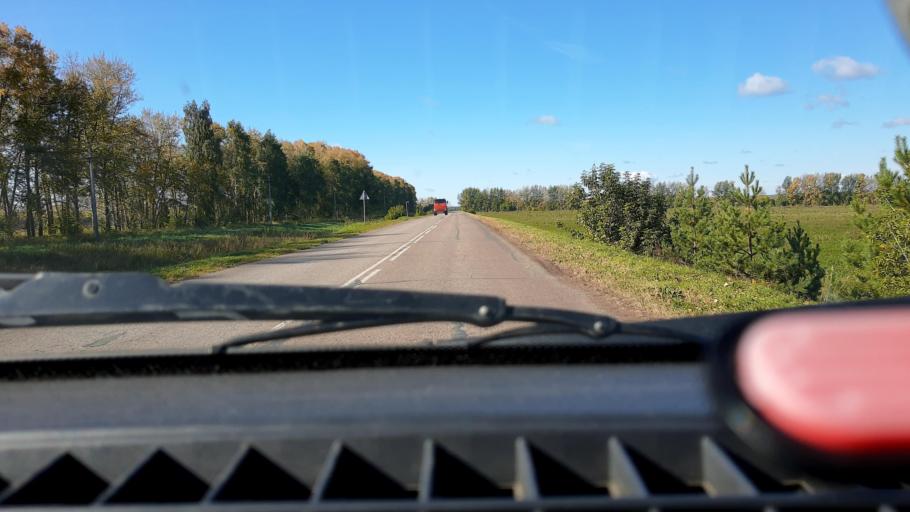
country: RU
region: Bashkortostan
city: Kushnarenkovo
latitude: 55.0632
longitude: 55.4450
